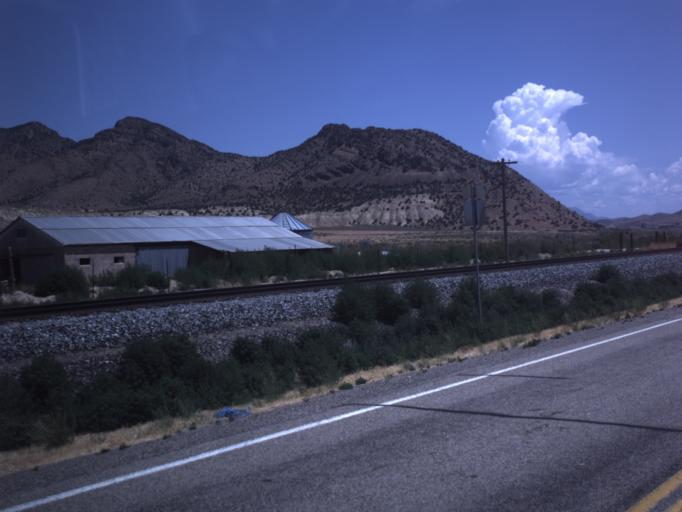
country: US
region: Utah
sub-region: Millard County
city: Delta
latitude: 39.5360
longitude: -112.2742
